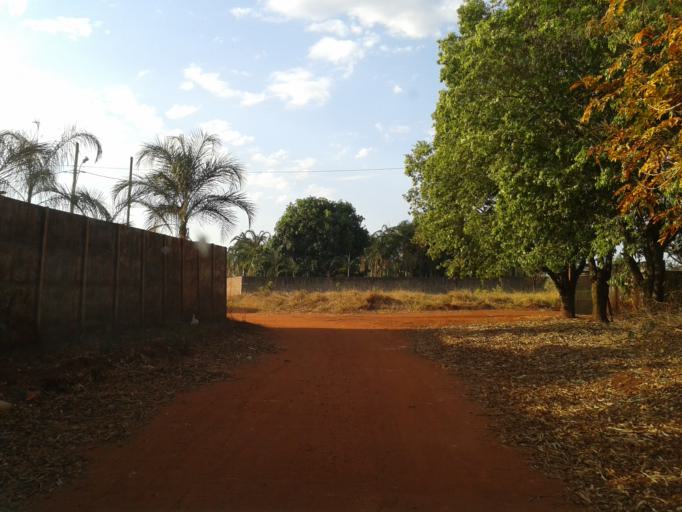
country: BR
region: Minas Gerais
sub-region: Ituiutaba
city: Ituiutaba
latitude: -18.9972
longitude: -49.4356
